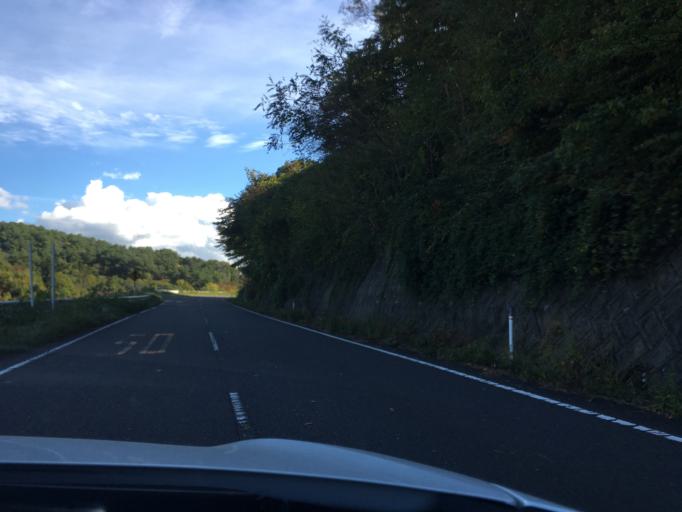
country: JP
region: Fukushima
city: Ishikawa
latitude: 37.1528
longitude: 140.5959
